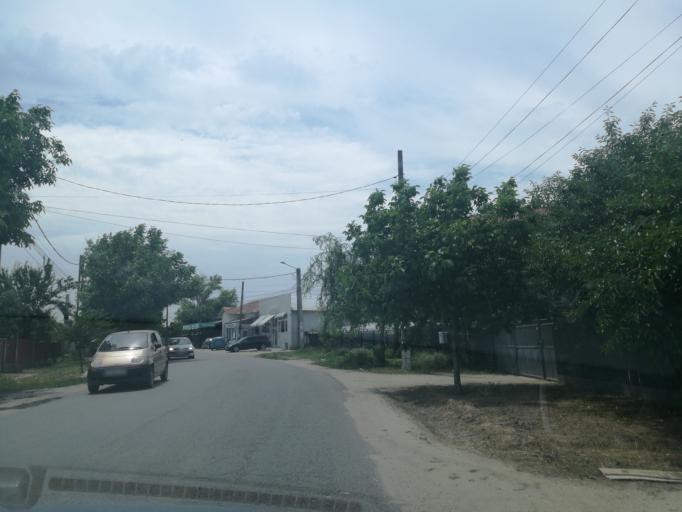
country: RO
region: Ilfov
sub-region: Comuna Vidra
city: Vidra
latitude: 44.2655
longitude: 26.1525
